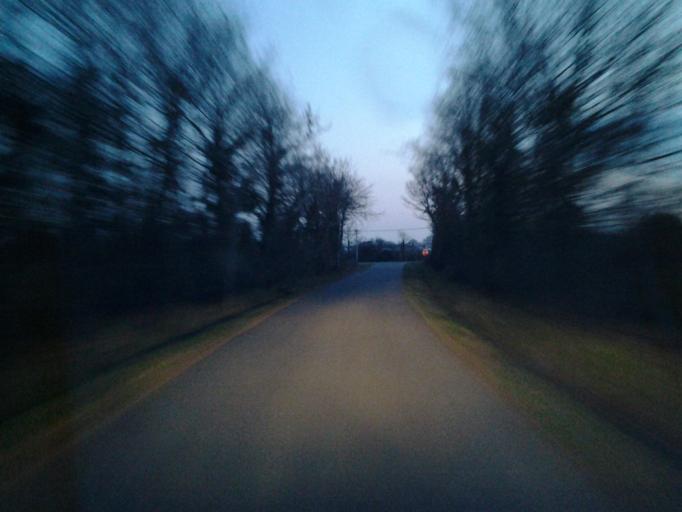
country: FR
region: Pays de la Loire
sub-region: Departement de la Vendee
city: Saint-Florent-des-Bois
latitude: 46.5685
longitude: -1.3387
